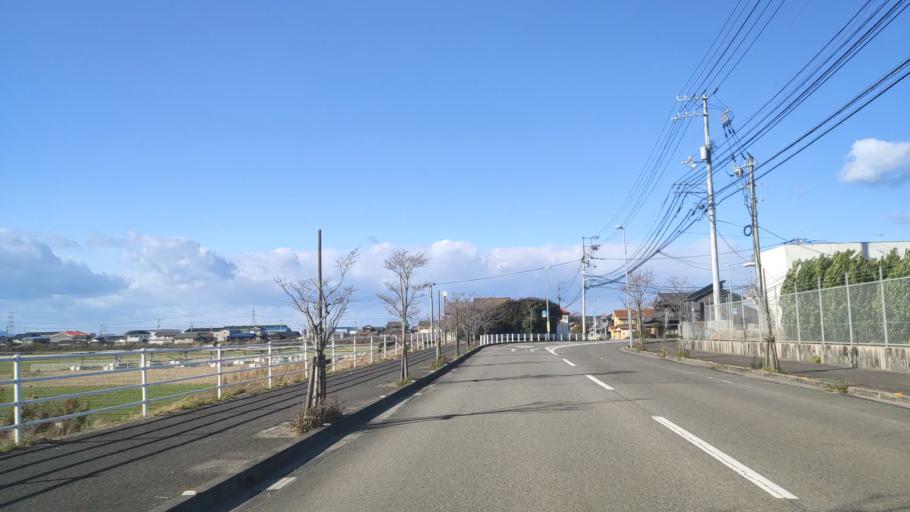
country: JP
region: Ehime
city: Saijo
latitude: 33.9278
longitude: 133.1657
